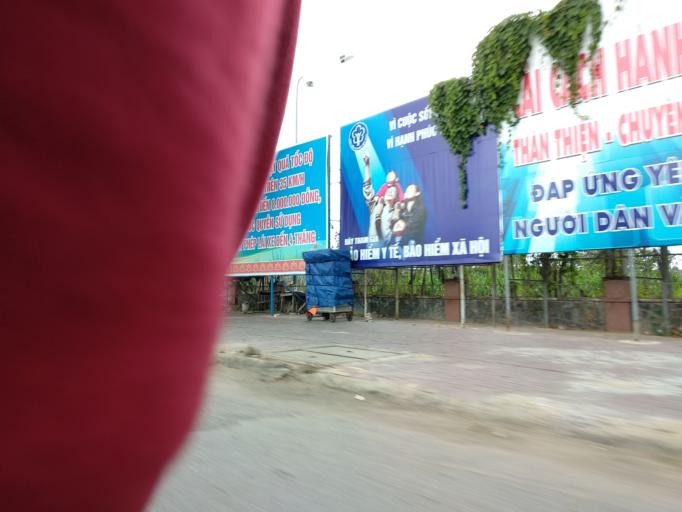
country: VN
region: Dong Nai
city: Nhon Trach
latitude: 10.7238
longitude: 106.8852
